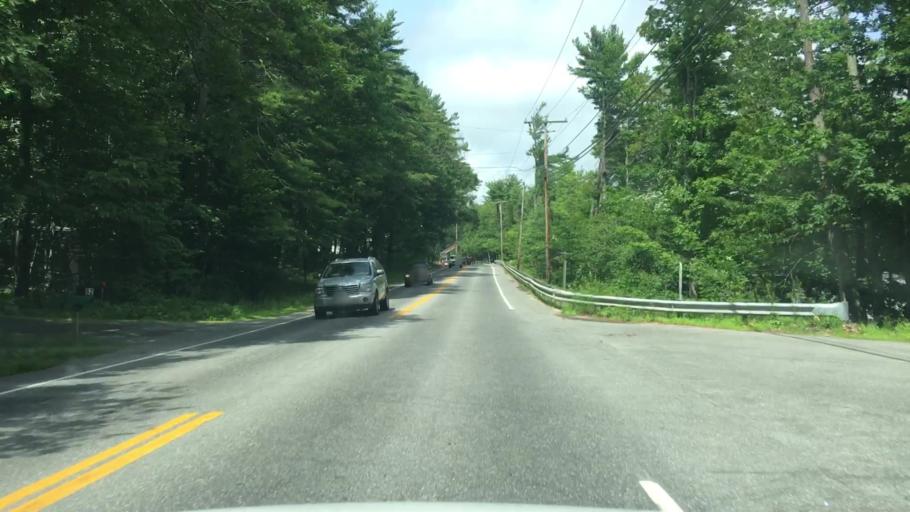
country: US
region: Maine
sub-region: Cumberland County
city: Brunswick
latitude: 43.8534
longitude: -69.9129
